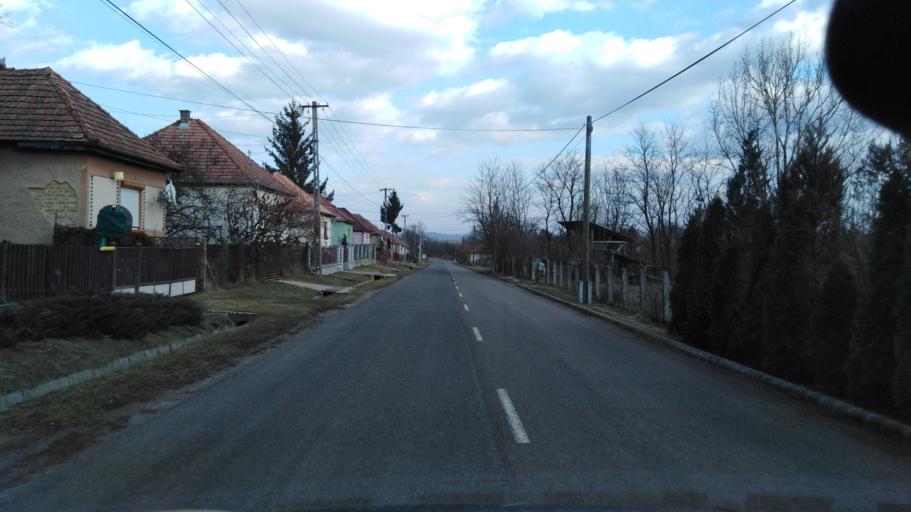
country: HU
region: Nograd
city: Matranovak
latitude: 48.1490
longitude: 19.9550
